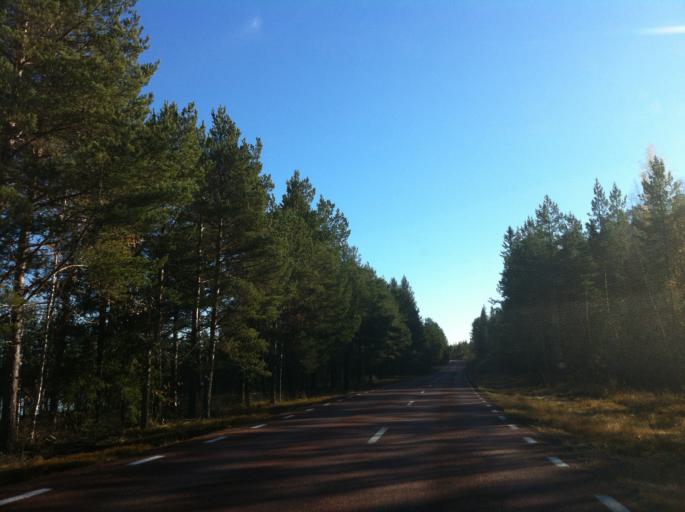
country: SE
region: Dalarna
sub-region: Alvdalens Kommun
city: AElvdalen
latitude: 61.3038
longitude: 13.7257
